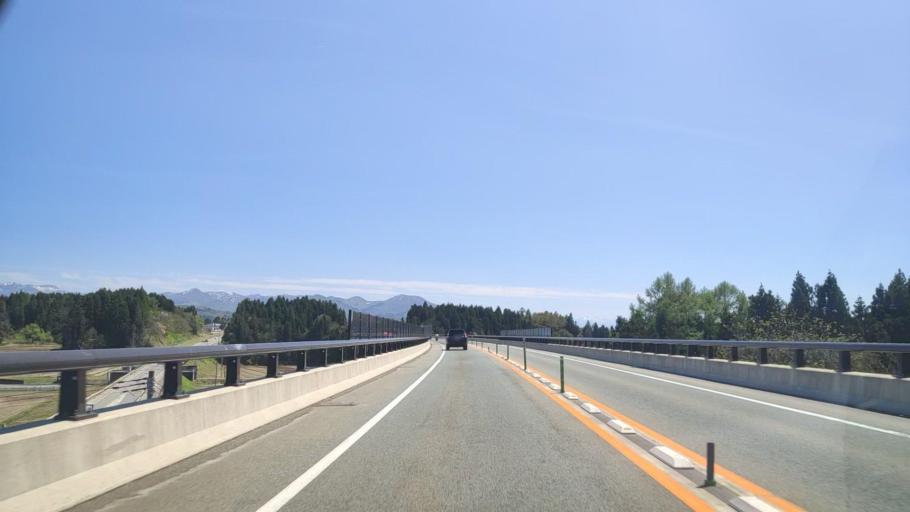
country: JP
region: Yamagata
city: Obanazawa
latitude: 38.6322
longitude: 140.3731
